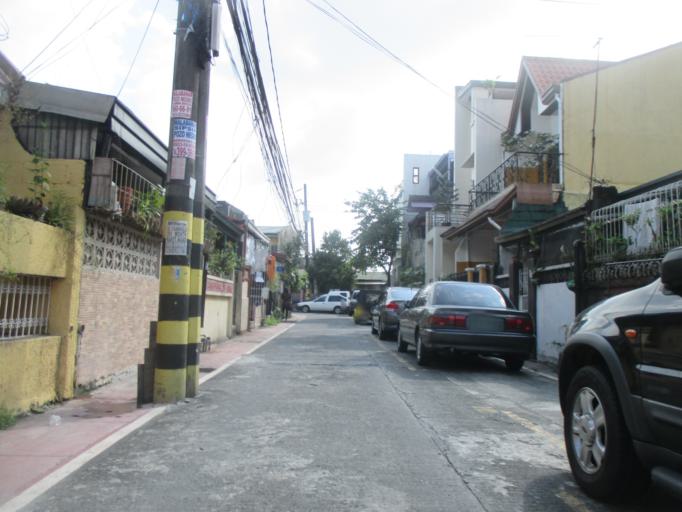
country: PH
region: Metro Manila
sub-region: Marikina
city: Calumpang
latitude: 14.6339
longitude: 121.0816
